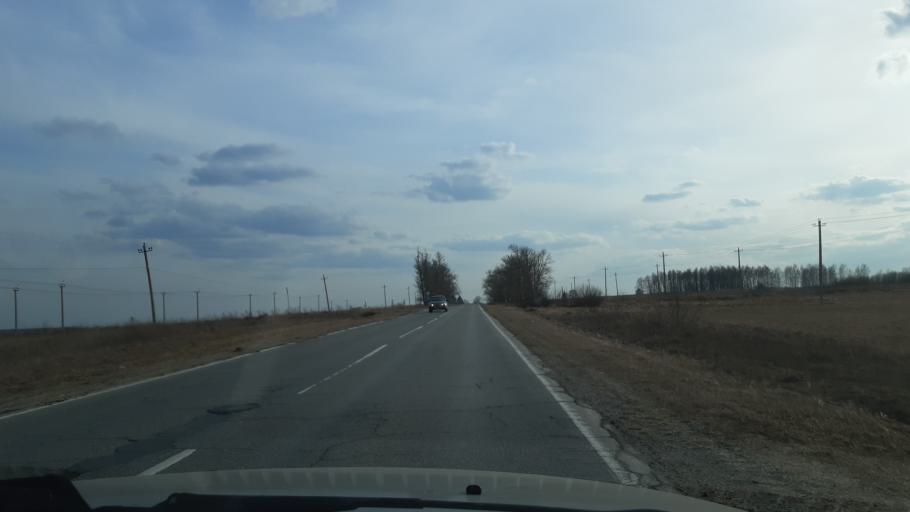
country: RU
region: Vladimir
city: Nikologory
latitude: 56.1672
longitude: 41.9986
